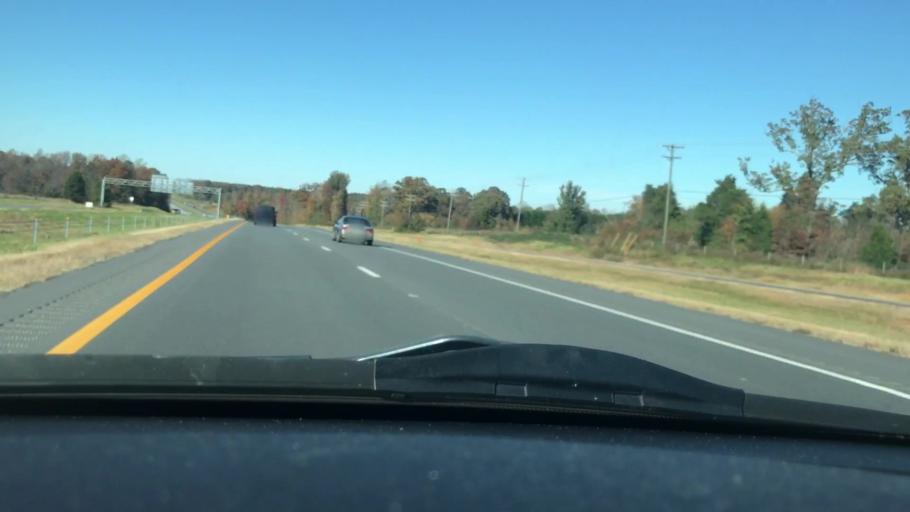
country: US
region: North Carolina
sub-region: Guilford County
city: Summerfield
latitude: 36.2489
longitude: -79.9212
